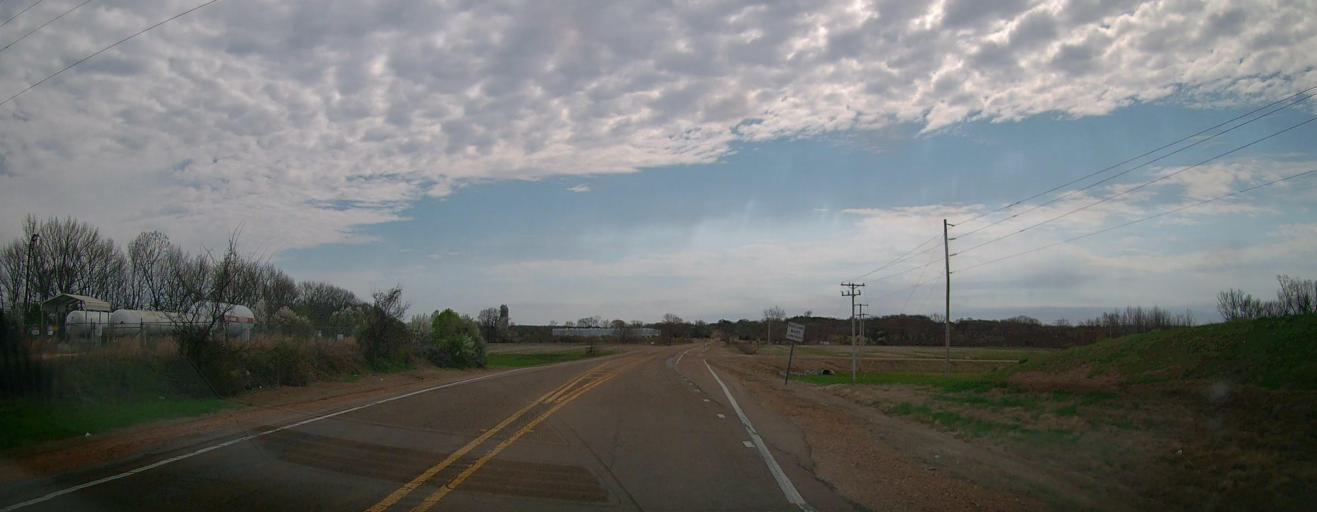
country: US
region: Mississippi
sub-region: Marshall County
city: Byhalia
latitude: 34.8682
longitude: -89.6686
